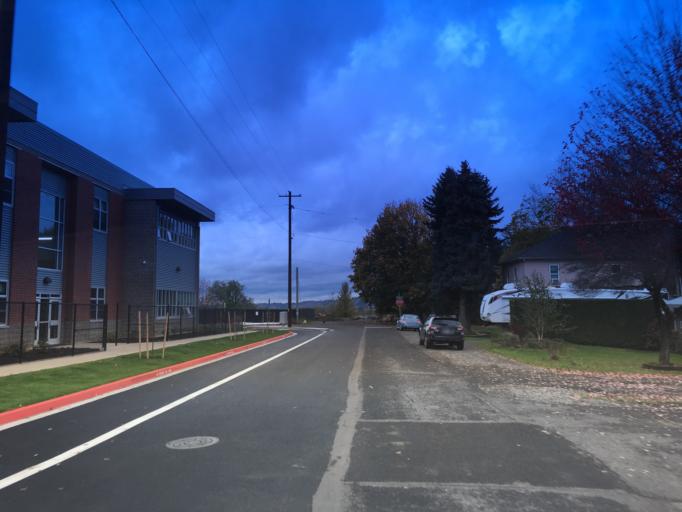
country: US
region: Oregon
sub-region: Multnomah County
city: Fairview
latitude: 45.5402
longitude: -122.4345
